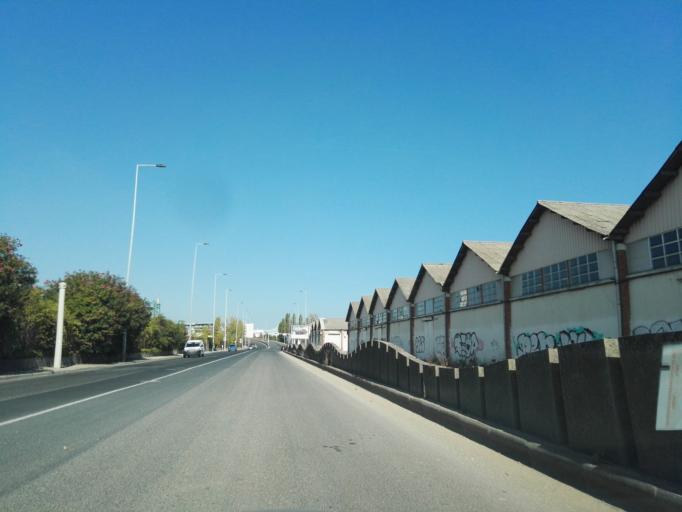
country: PT
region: Lisbon
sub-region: Loures
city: Moscavide
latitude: 38.7493
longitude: -9.0965
